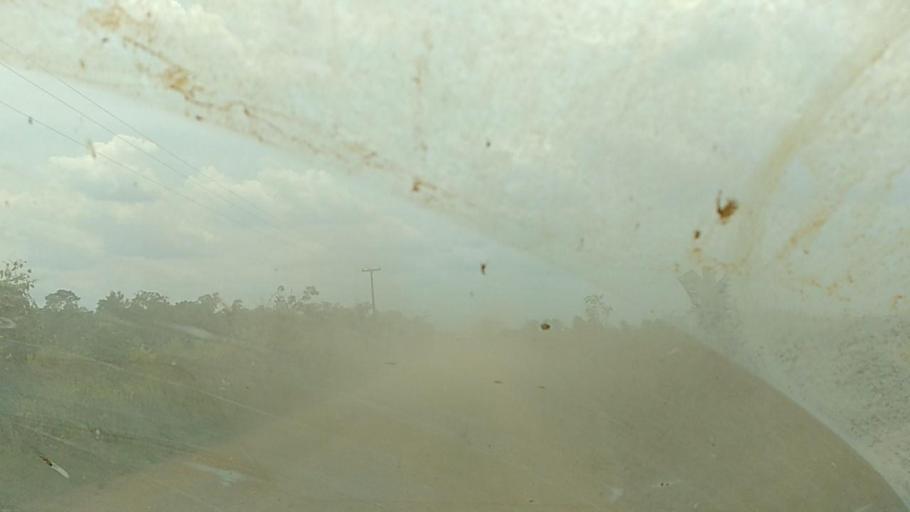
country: BR
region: Rondonia
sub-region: Porto Velho
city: Porto Velho
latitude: -8.9482
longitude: -64.3121
